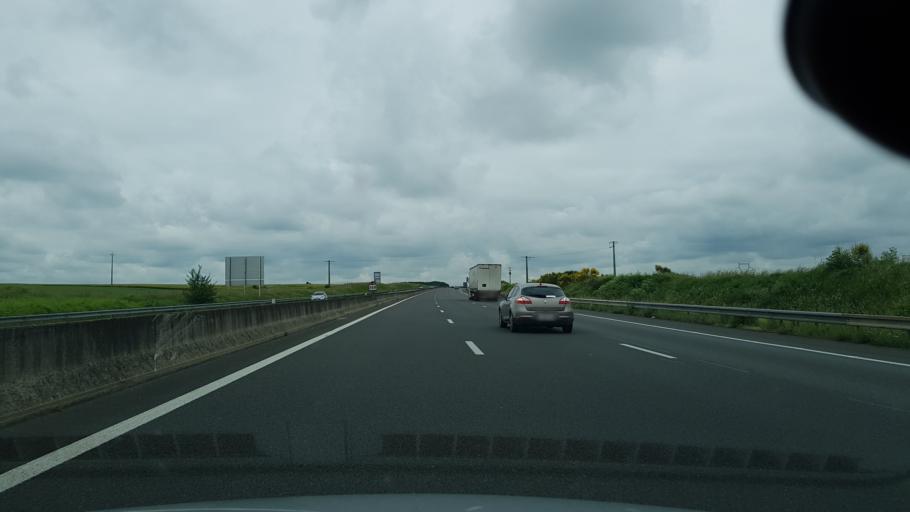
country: FR
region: Centre
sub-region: Departement du Loir-et-Cher
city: Saint-Sulpice-de-Pommeray
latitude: 47.6171
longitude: 1.2145
